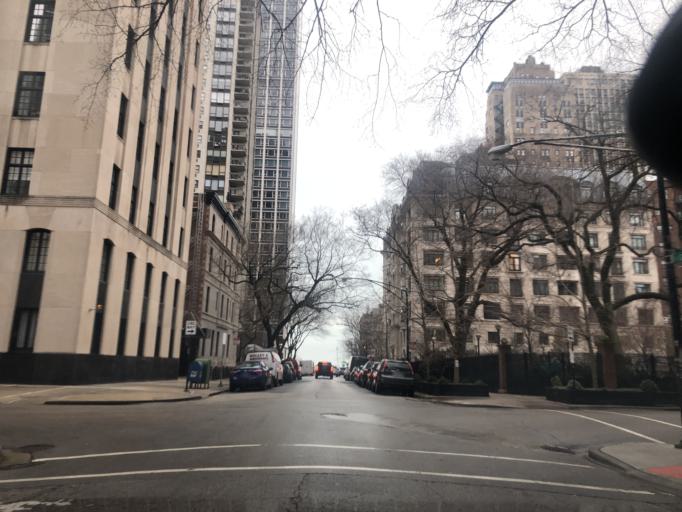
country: US
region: Illinois
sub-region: Cook County
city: Chicago
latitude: 41.9057
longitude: -87.6276
